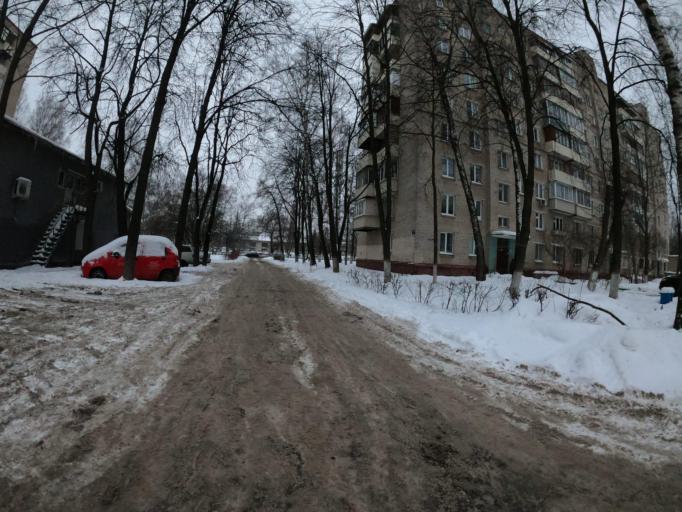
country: RU
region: Moskovskaya
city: Dubrovitsy
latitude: 55.4220
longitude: 37.5067
